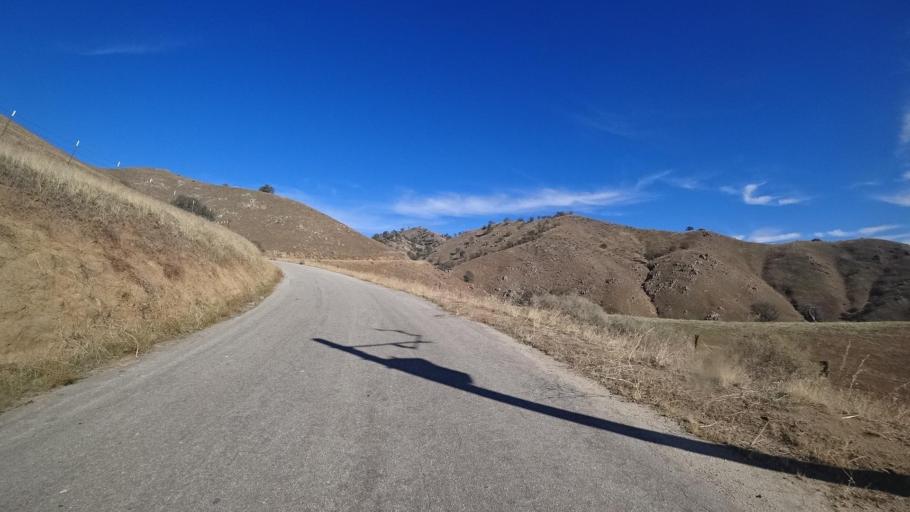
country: US
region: California
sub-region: Kern County
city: Arvin
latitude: 35.4248
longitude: -118.7299
